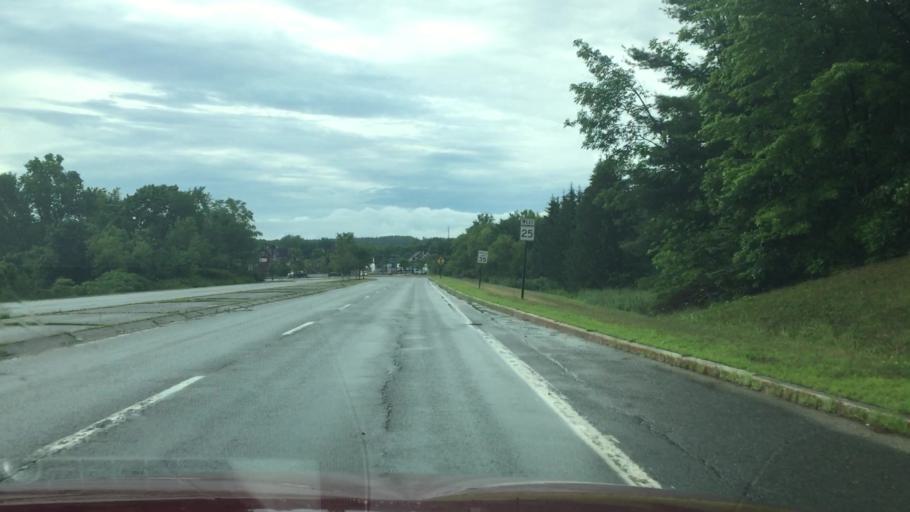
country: US
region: Maine
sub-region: Cumberland County
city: Westbrook
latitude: 43.6761
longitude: -70.3529
